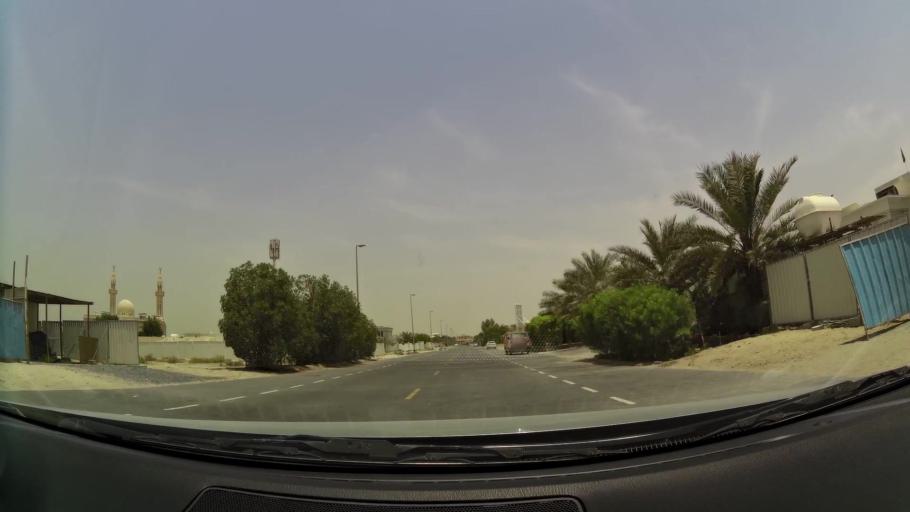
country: AE
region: Ash Shariqah
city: Sharjah
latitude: 25.2061
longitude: 55.3789
